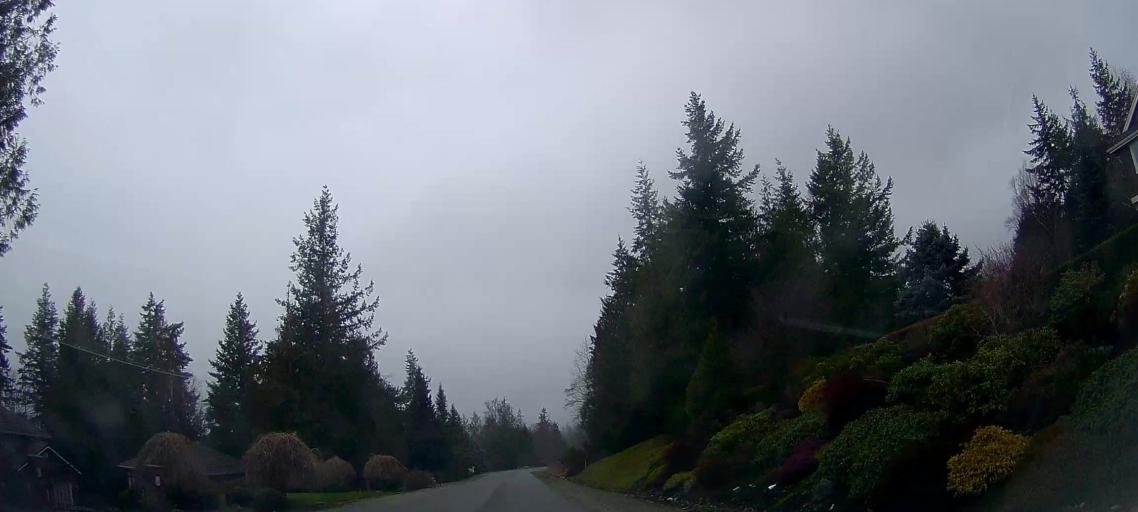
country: US
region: Washington
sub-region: Skagit County
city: Big Lake
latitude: 48.3735
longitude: -122.2944
